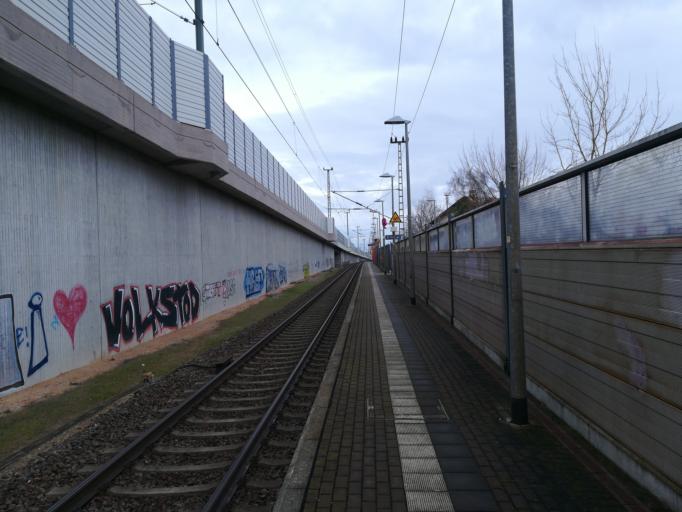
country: DE
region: Saxony-Anhalt
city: Schkopau
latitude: 51.4235
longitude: 11.9881
